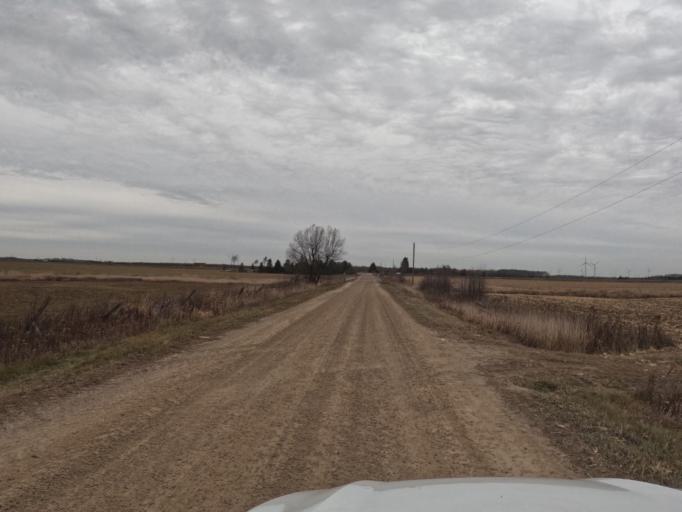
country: CA
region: Ontario
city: Shelburne
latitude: 44.0360
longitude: -80.3724
